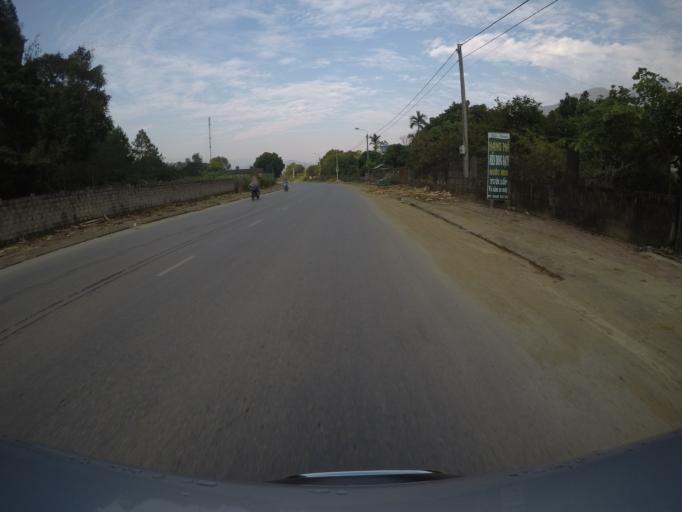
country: VN
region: Lai Chau
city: Tam Duong
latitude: 22.3184
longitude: 103.6570
